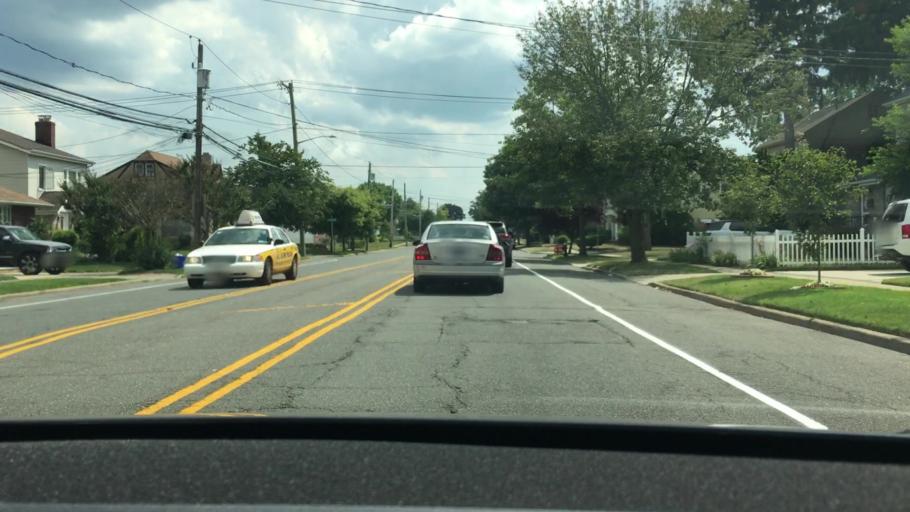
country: US
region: New York
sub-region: Nassau County
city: Valley Stream
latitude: 40.6712
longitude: -73.6950
